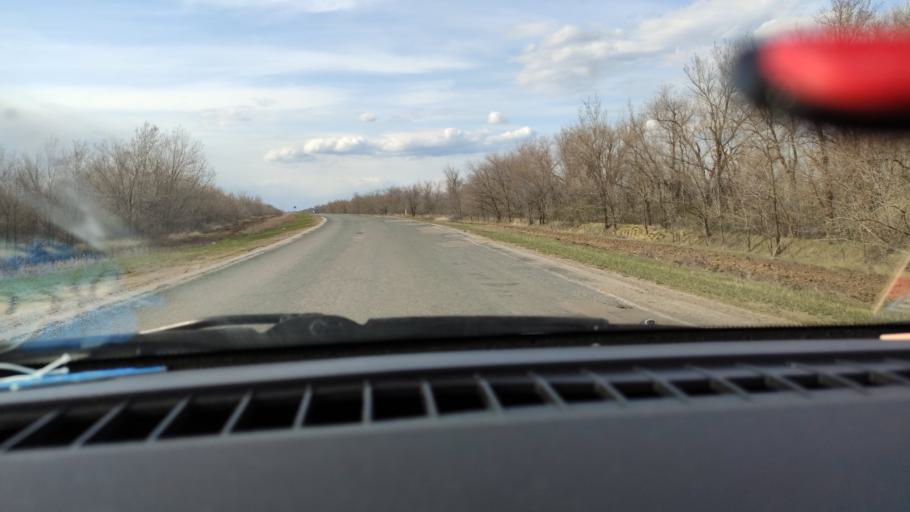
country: RU
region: Saratov
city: Rovnoye
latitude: 50.9826
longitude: 46.1146
